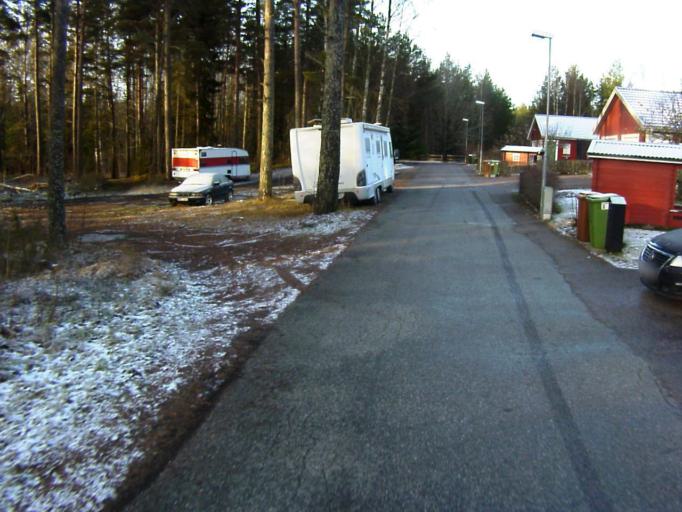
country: SE
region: Soedermanland
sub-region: Eskilstuna Kommun
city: Hallbybrunn
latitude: 59.3929
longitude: 16.4064
